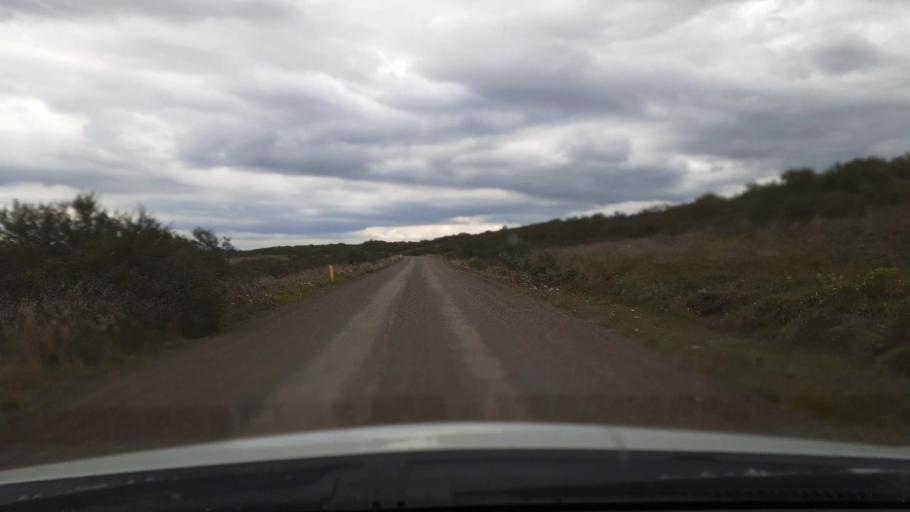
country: IS
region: West
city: Borgarnes
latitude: 64.6083
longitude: -21.9601
